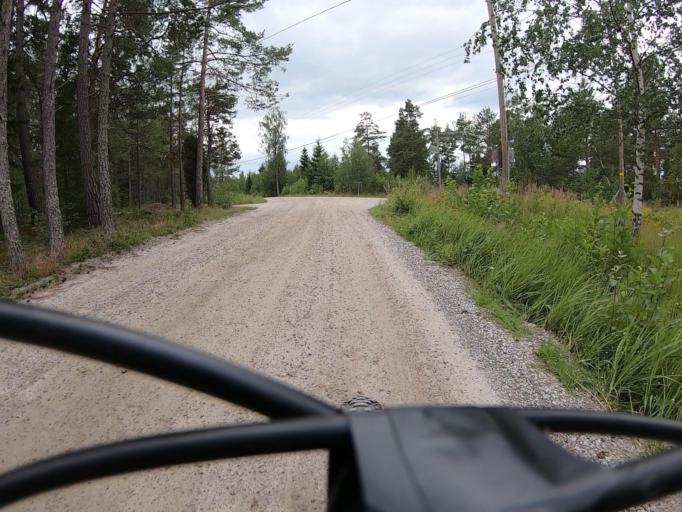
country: FI
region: Varsinais-Suomi
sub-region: Vakka-Suomi
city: Uusikaupunki
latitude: 60.8408
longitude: 21.3855
